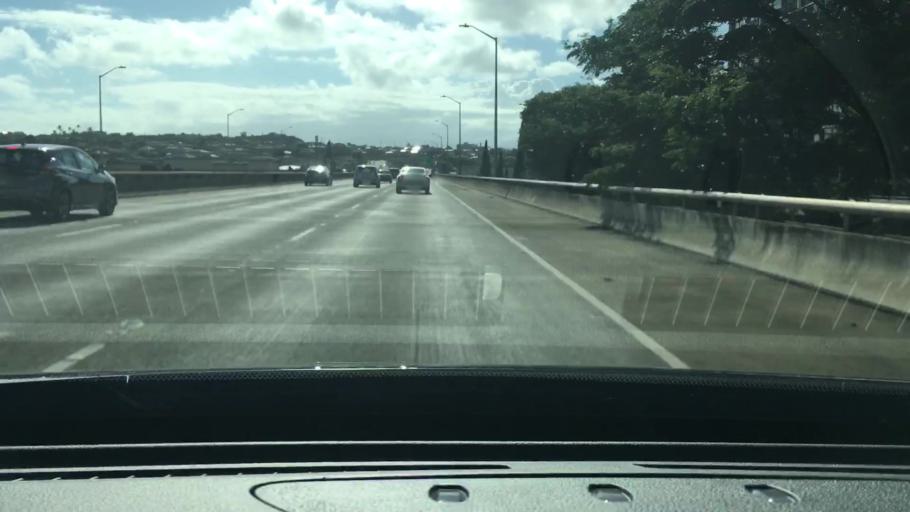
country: US
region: Hawaii
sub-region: Honolulu County
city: Honolulu
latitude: 21.2785
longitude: -157.7848
